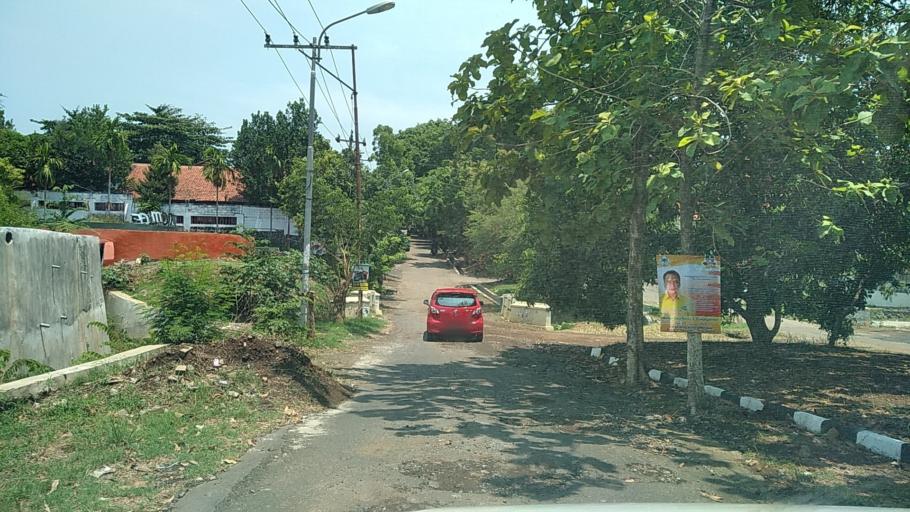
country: ID
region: Central Java
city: Semarang
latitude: -6.9967
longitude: 110.3494
